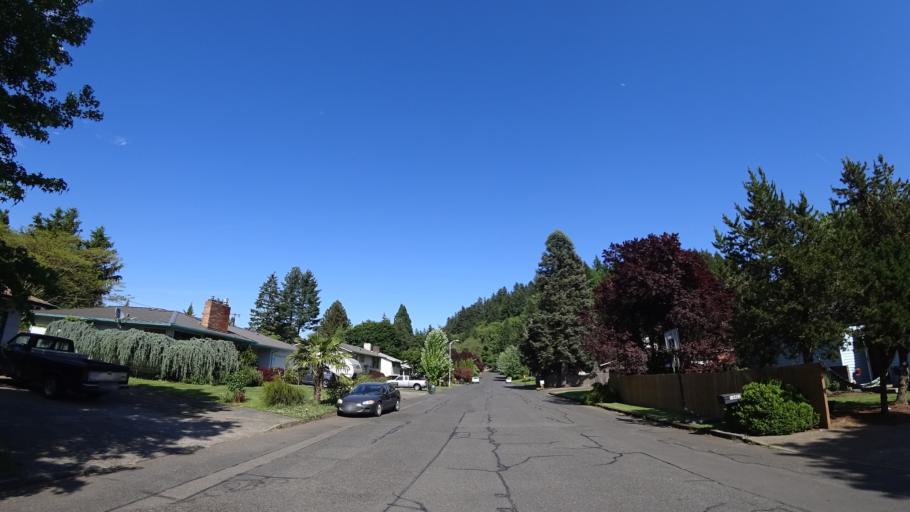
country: US
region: Oregon
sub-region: Multnomah County
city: Gresham
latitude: 45.5019
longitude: -122.4732
